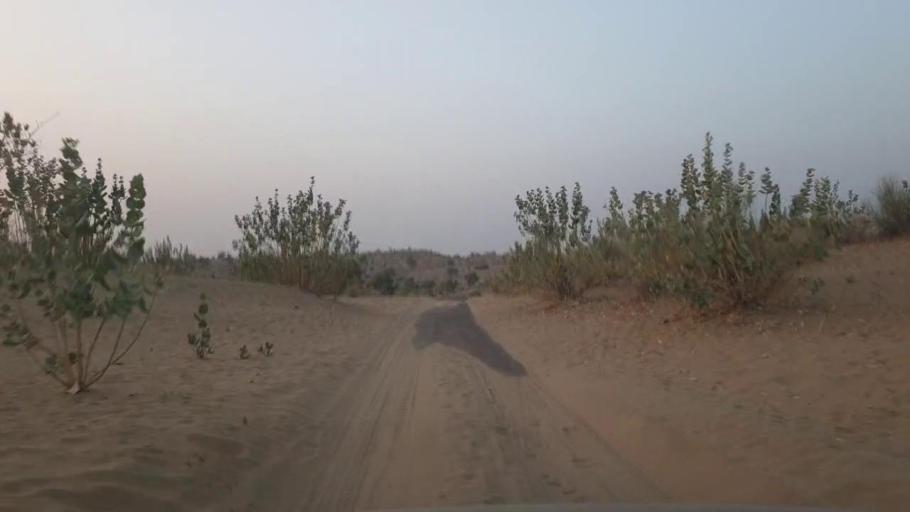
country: PK
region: Sindh
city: Umarkot
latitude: 25.3139
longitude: 70.0596
